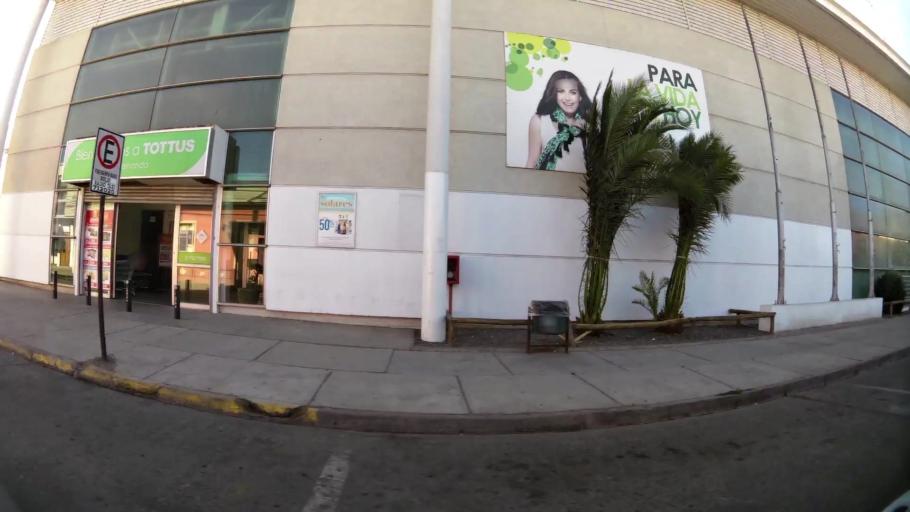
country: CL
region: O'Higgins
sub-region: Provincia de Colchagua
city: Chimbarongo
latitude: -34.5861
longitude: -70.9908
